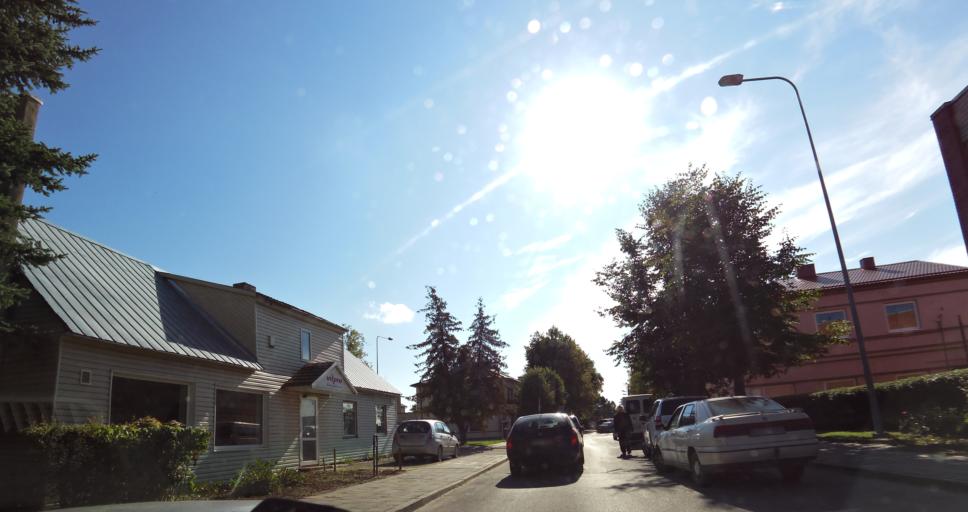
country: LT
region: Panevezys
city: Pasvalys
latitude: 56.0589
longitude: 24.4015
